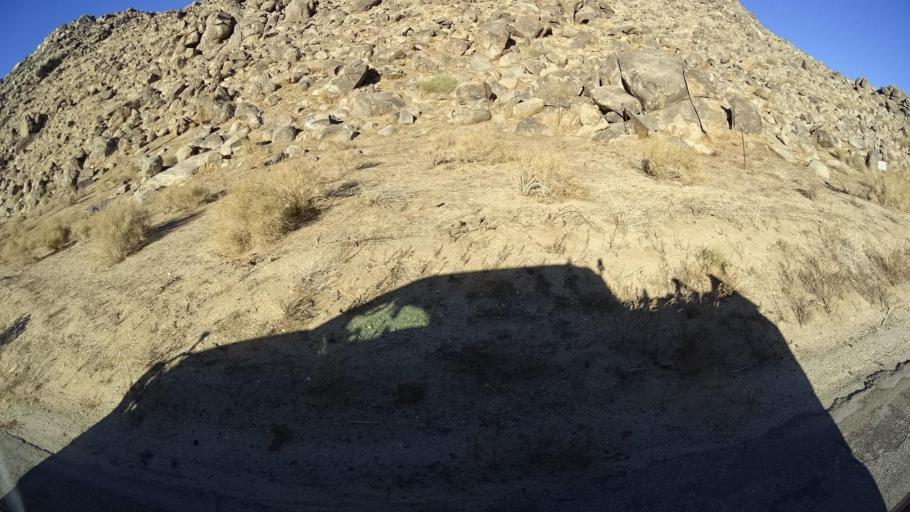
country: US
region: California
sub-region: Kern County
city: Weldon
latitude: 35.5618
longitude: -118.2372
